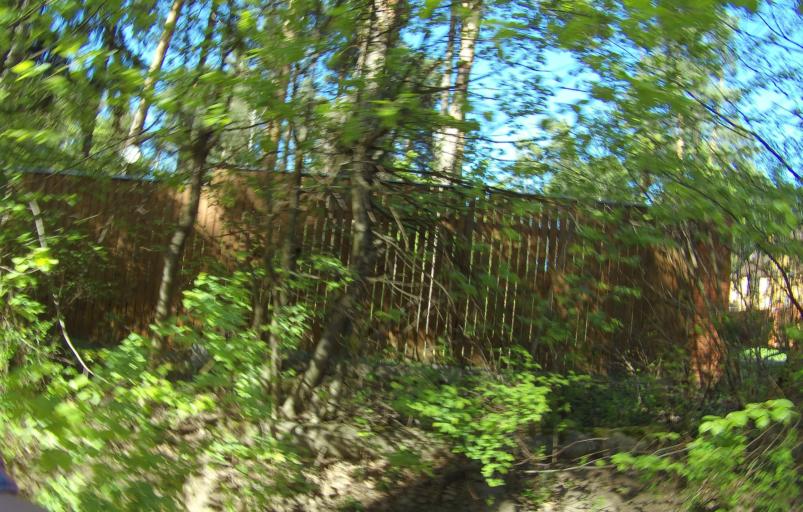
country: RU
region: Moskovskaya
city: Kratovo
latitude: 55.5792
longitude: 38.1777
